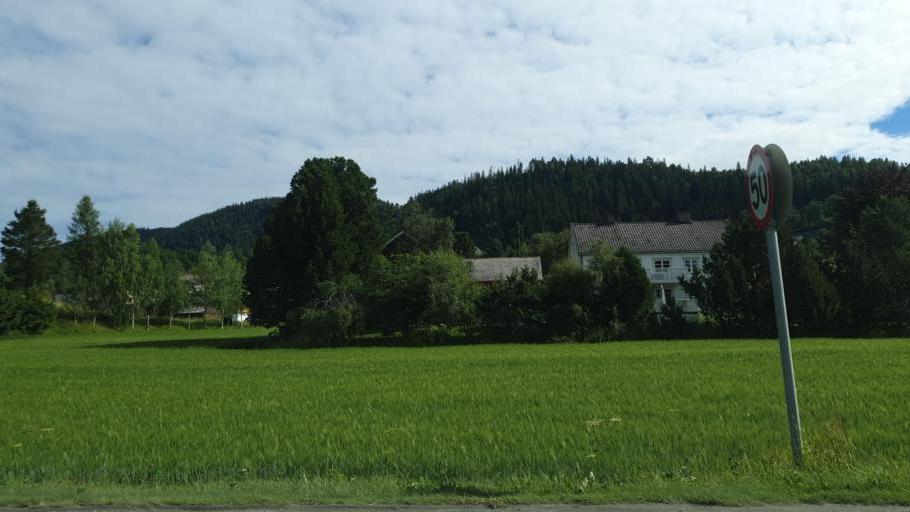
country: NO
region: Sor-Trondelag
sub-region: Melhus
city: Melhus
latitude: 63.2319
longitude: 10.2786
